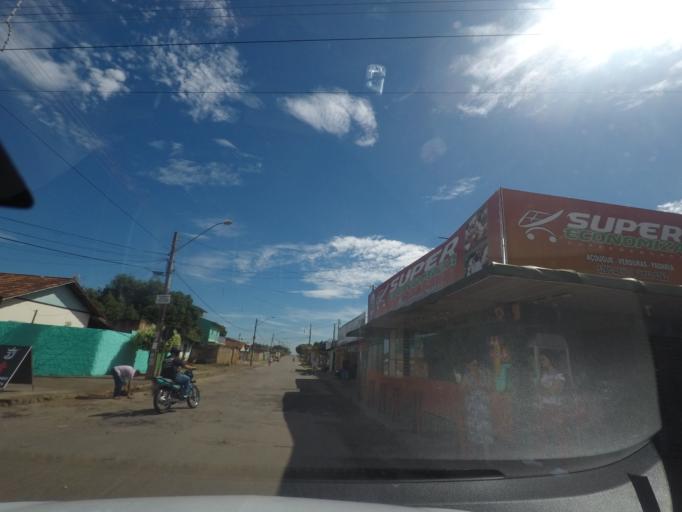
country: BR
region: Goias
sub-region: Aparecida De Goiania
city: Aparecida de Goiania
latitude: -16.8156
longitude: -49.2918
